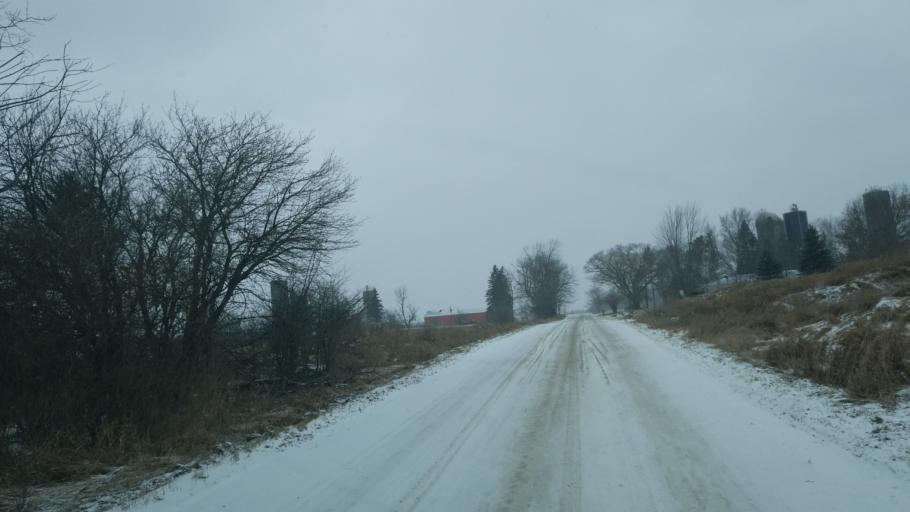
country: US
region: Michigan
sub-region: Osceola County
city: Evart
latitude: 44.0223
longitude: -85.2066
